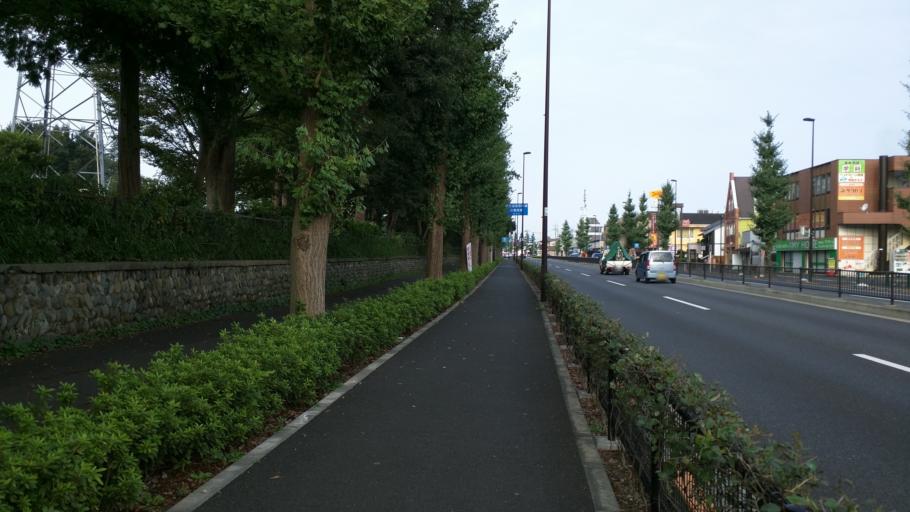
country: JP
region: Tokyo
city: Kokubunji
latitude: 35.6887
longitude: 139.5114
